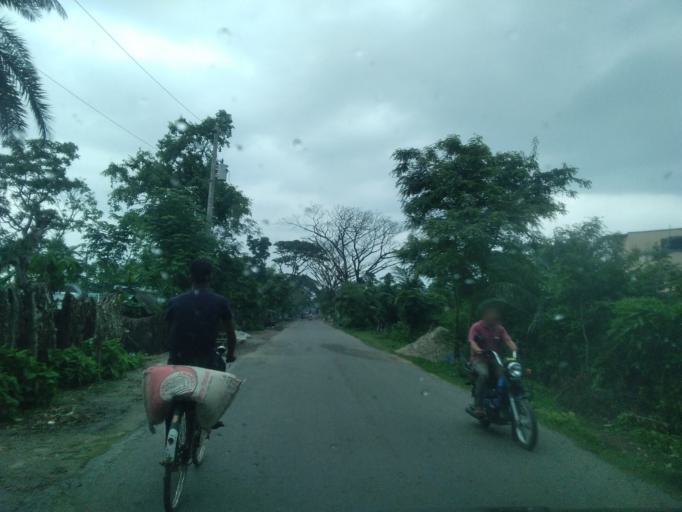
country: IN
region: West Bengal
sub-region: North 24 Parganas
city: Taki
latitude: 22.5047
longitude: 89.0127
